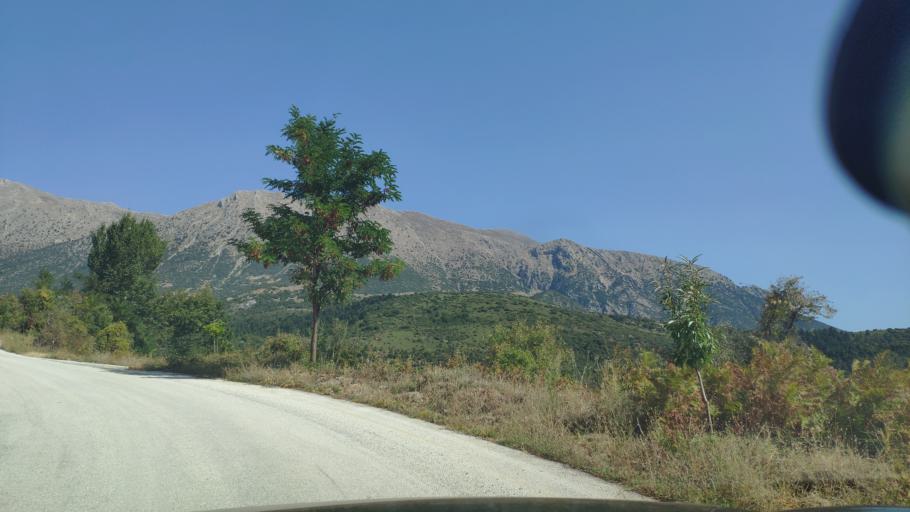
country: GR
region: Peloponnese
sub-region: Nomos Korinthias
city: Nemea
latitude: 37.8678
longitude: 22.3869
